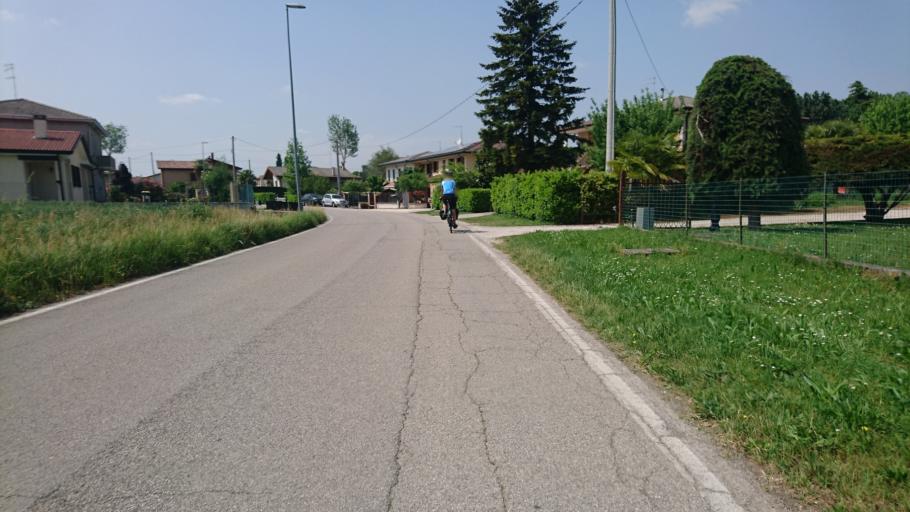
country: IT
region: Veneto
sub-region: Provincia di Venezia
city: Camponogara
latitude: 45.3737
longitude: 12.0975
